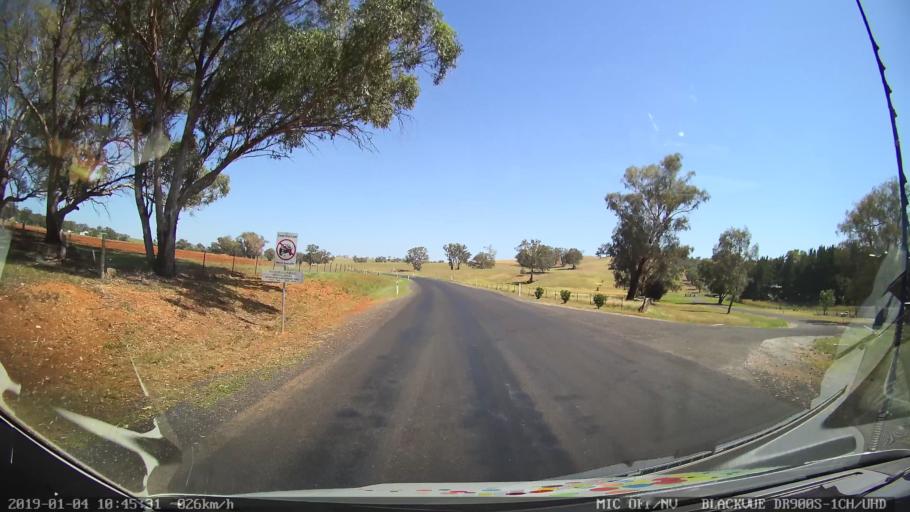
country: AU
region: New South Wales
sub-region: Cabonne
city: Molong
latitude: -33.2881
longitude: 148.7294
